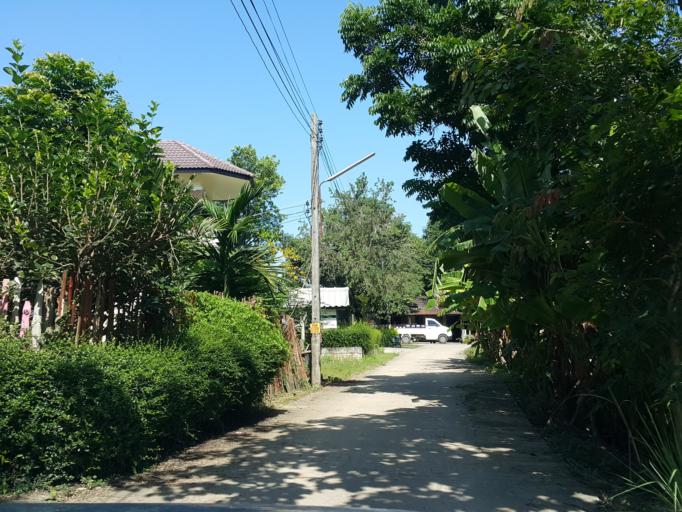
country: TH
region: Chiang Mai
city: San Kamphaeng
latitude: 18.7464
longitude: 99.1701
